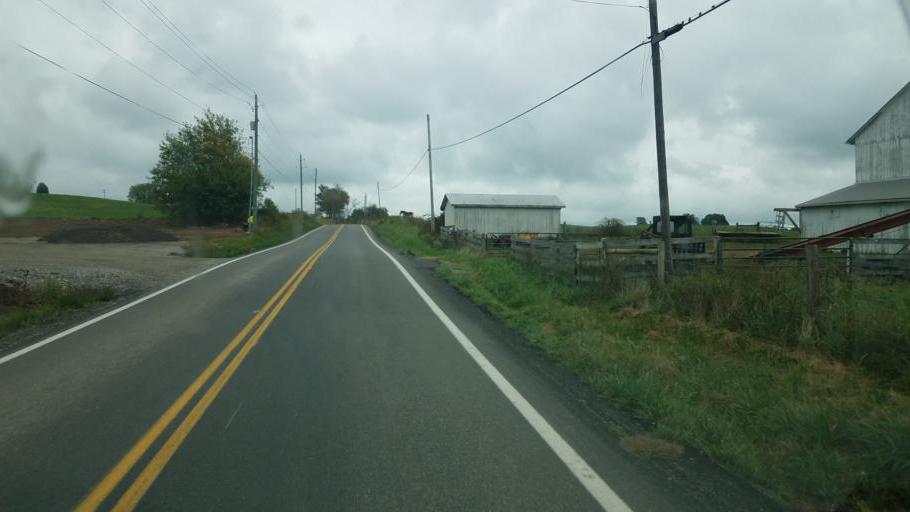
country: US
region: Ohio
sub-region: Holmes County
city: Millersburg
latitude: 40.6118
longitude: -81.8295
